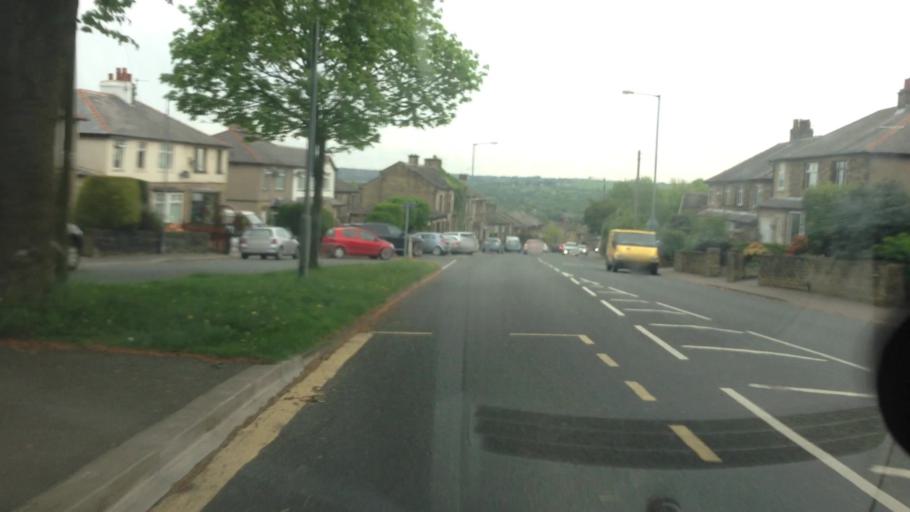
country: GB
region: England
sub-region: Calderdale
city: Brighouse
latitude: 53.6886
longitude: -1.7943
